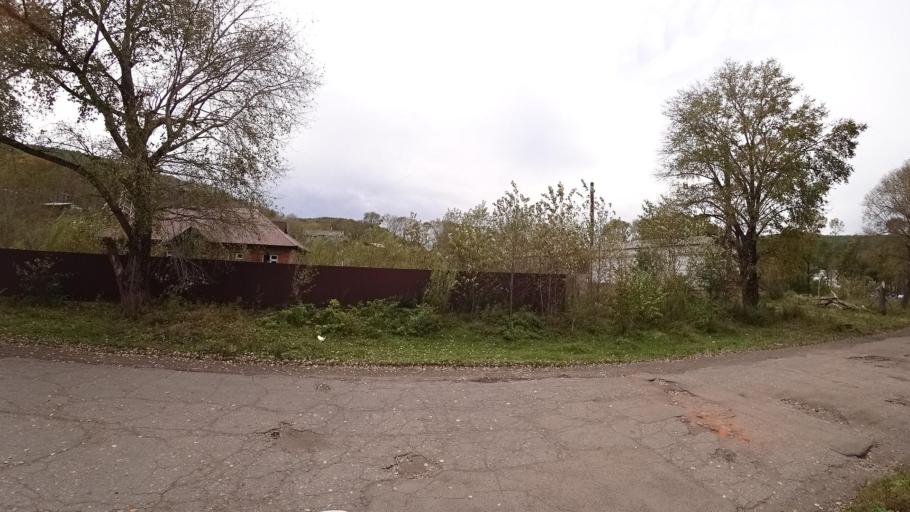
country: RU
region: Jewish Autonomous Oblast
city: Khingansk
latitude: 49.1270
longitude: 131.1967
